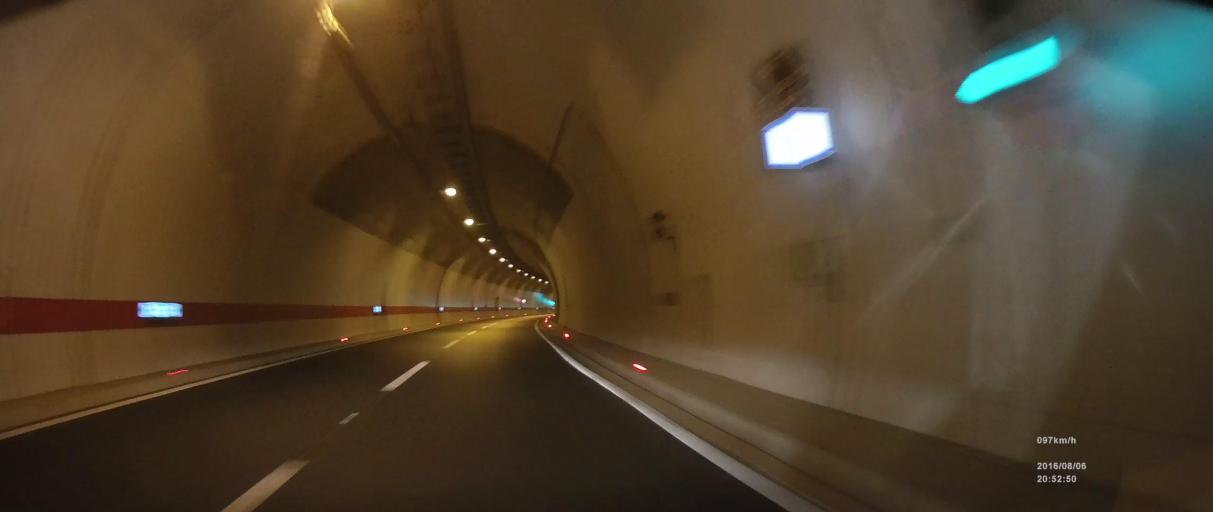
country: BA
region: Federation of Bosnia and Herzegovina
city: Ljubuski
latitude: 43.1367
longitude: 17.4829
